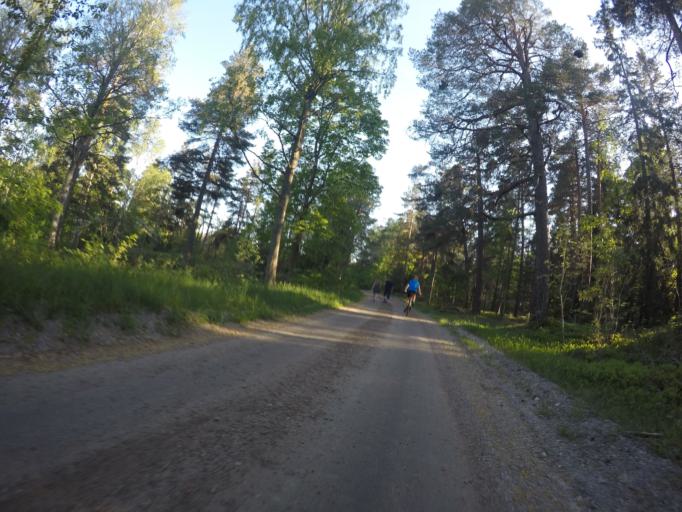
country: SE
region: Soedermanland
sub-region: Eskilstuna Kommun
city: Eskilstuna
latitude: 59.3478
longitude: 16.5331
